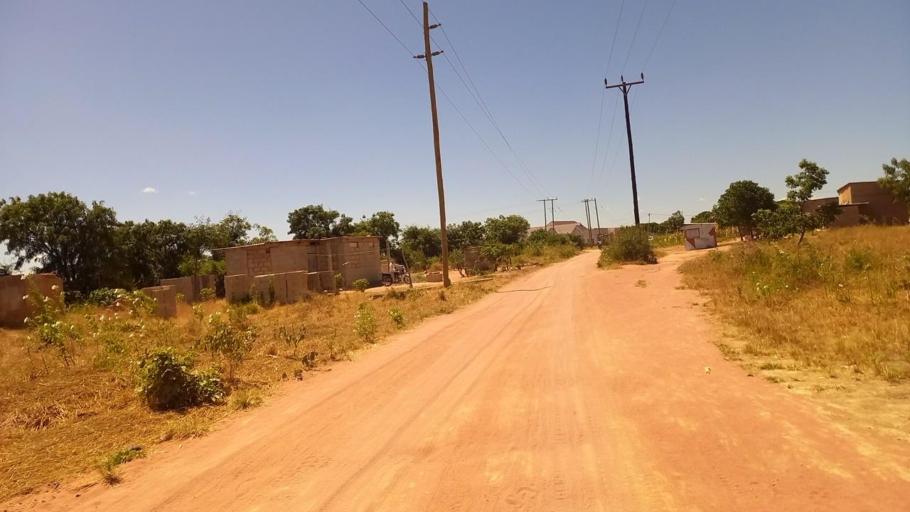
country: TZ
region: Dodoma
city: Dodoma
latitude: -6.1300
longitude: 35.7278
